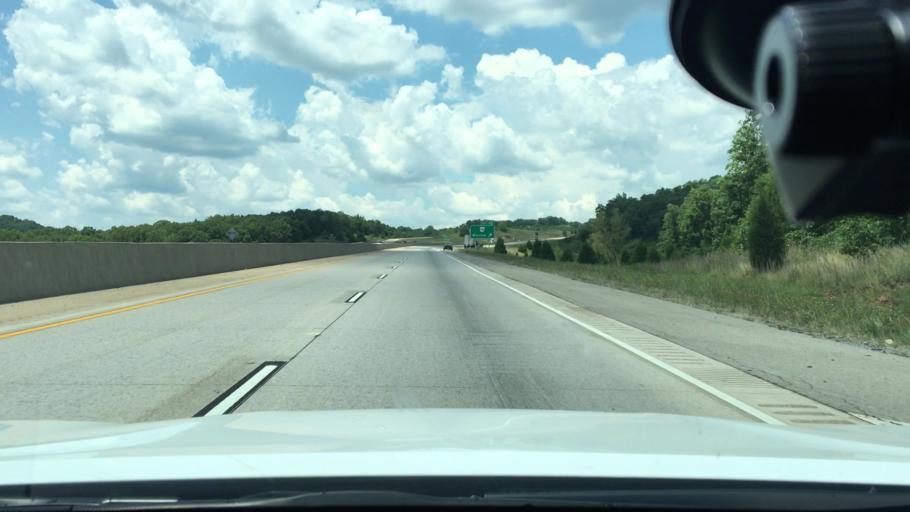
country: US
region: Arkansas
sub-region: Washington County
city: West Fork
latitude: 35.8102
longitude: -94.1900
